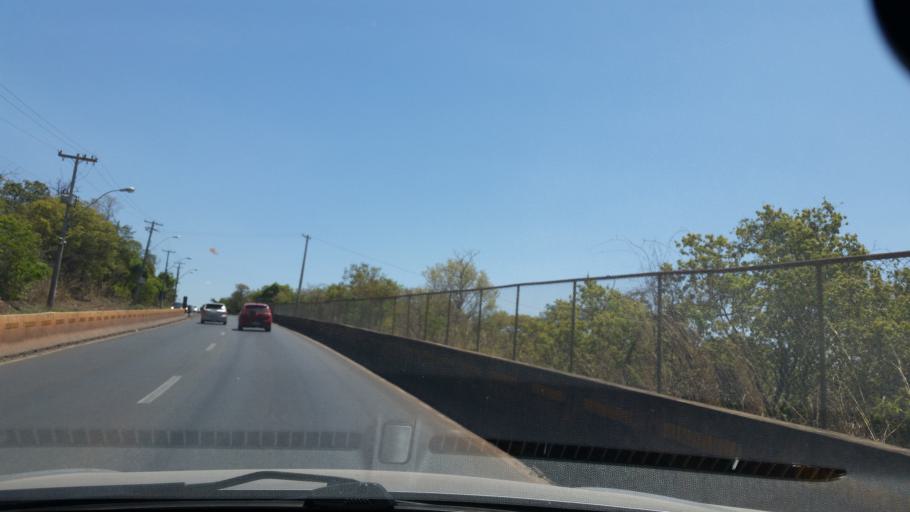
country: BR
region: Federal District
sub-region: Brasilia
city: Brasilia
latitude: -15.8010
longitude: -47.7913
